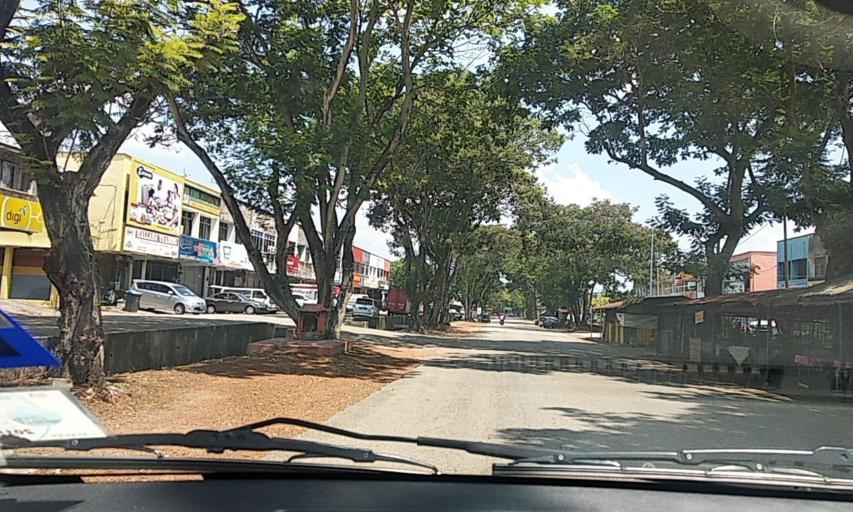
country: MY
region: Kedah
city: Sungai Petani
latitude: 5.6207
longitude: 100.4735
